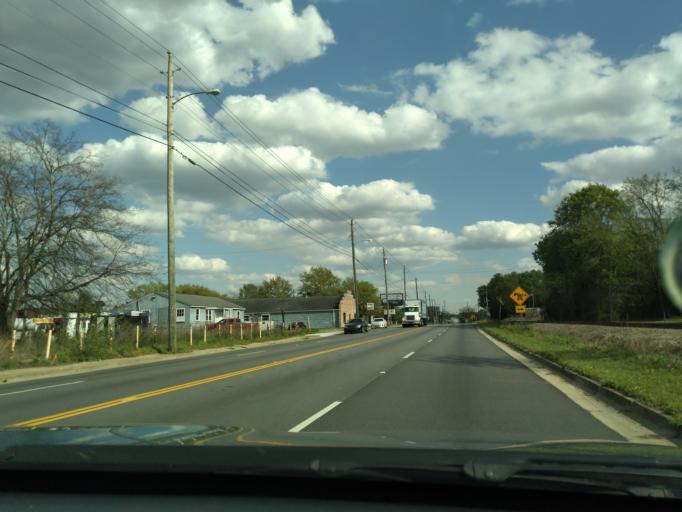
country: US
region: South Carolina
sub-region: Florence County
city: Florence
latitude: 34.2091
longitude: -79.7740
